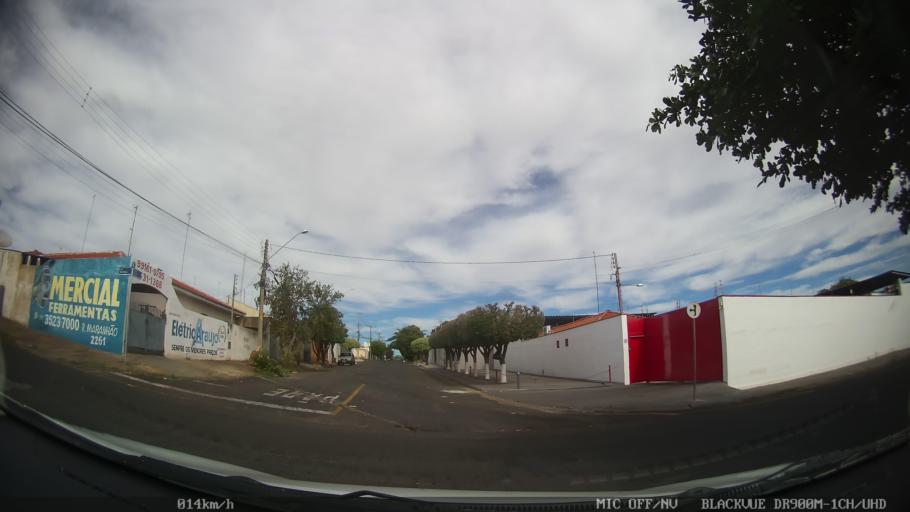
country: BR
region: Sao Paulo
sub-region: Catanduva
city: Catanduva
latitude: -21.1482
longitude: -48.9719
